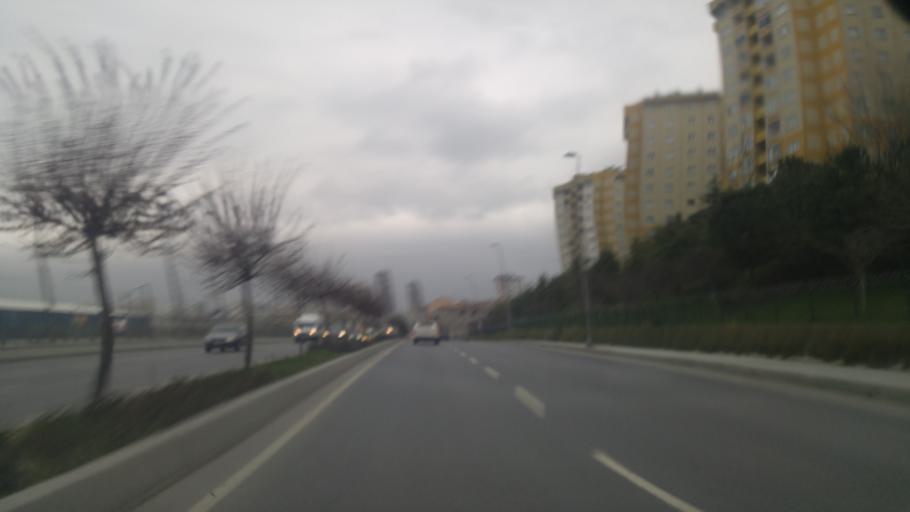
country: TR
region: Istanbul
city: Mahmutbey
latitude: 41.0269
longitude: 28.7678
